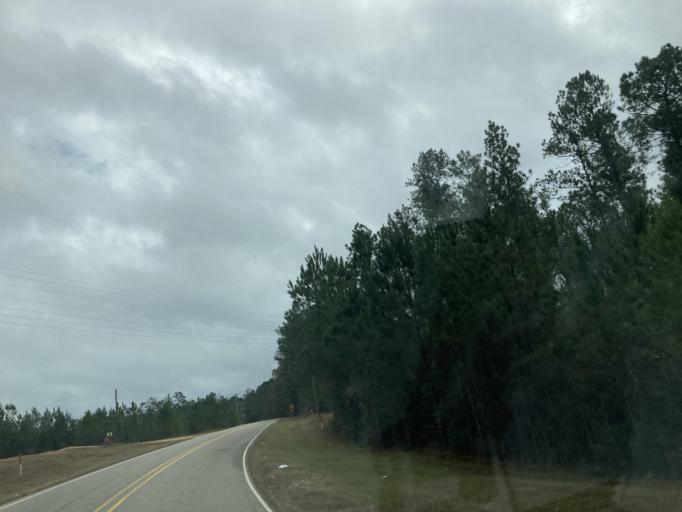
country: US
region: Mississippi
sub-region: Lamar County
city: Lumberton
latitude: 31.0662
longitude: -89.6154
